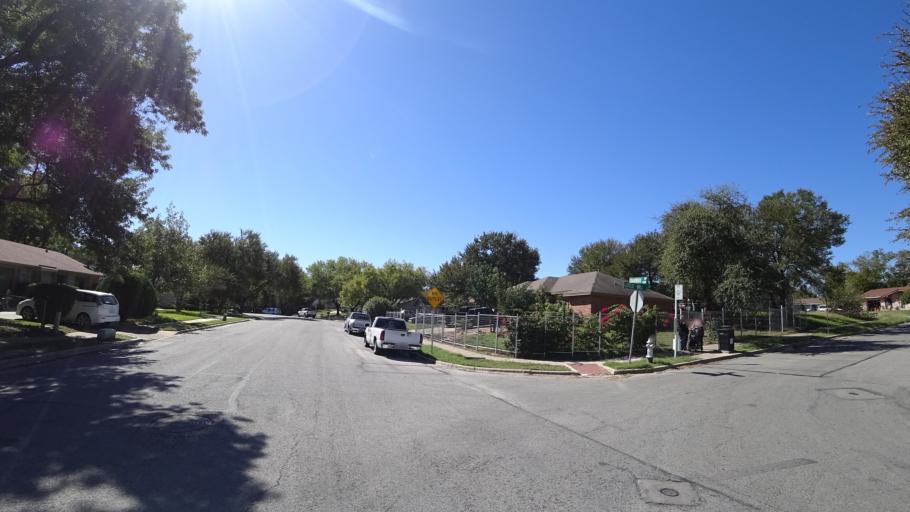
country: US
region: Texas
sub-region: Travis County
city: Austin
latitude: 30.2806
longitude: -97.6607
